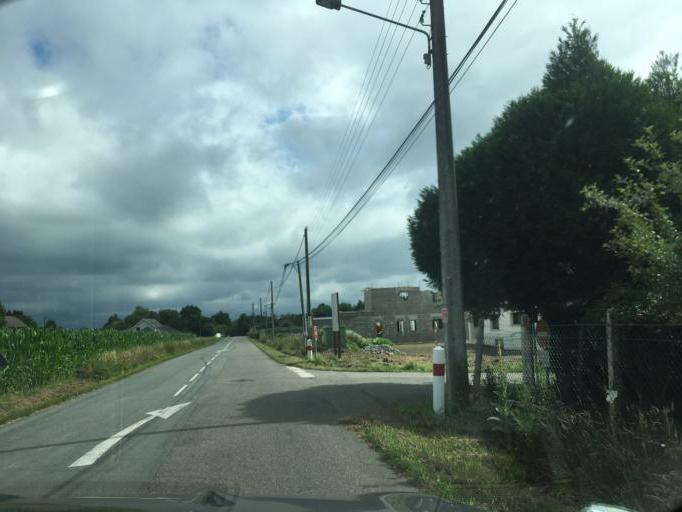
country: FR
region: Aquitaine
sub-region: Departement des Pyrenees-Atlantiques
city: Ousse
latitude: 43.3078
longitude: -0.2756
